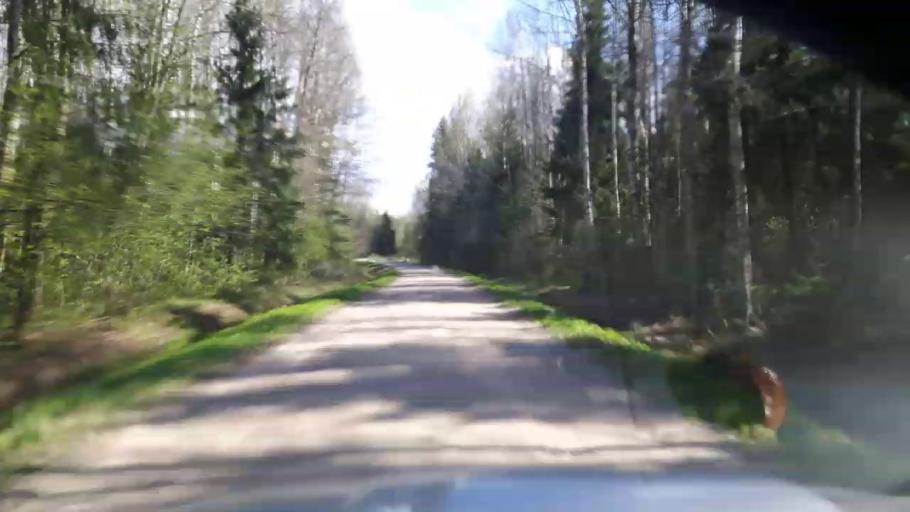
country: EE
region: Paernumaa
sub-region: Tootsi vald
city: Tootsi
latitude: 58.4536
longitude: 24.8192
